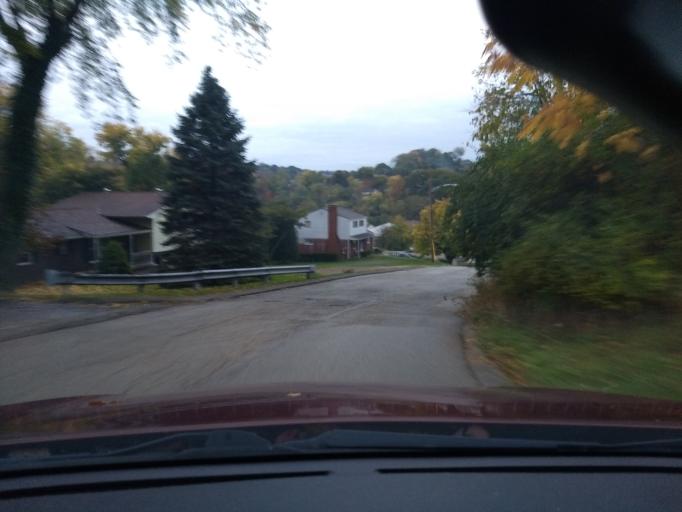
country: US
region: Pennsylvania
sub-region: Allegheny County
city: Pleasant Hills
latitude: 40.3505
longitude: -79.9598
